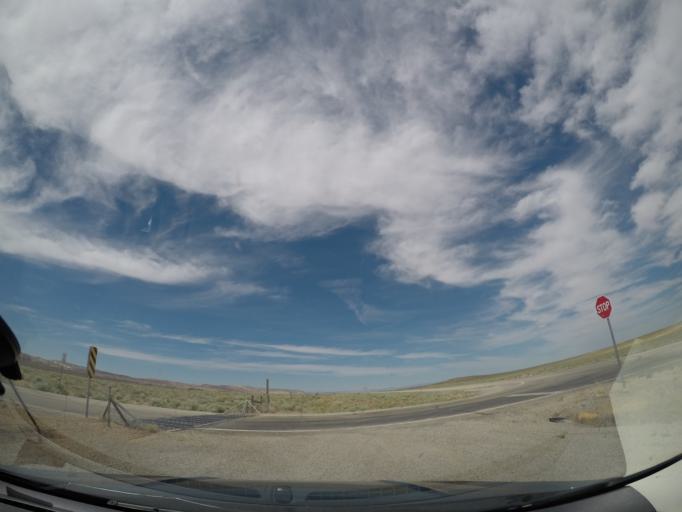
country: US
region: Utah
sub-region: Emery County
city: Ferron
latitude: 38.6306
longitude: -110.5669
